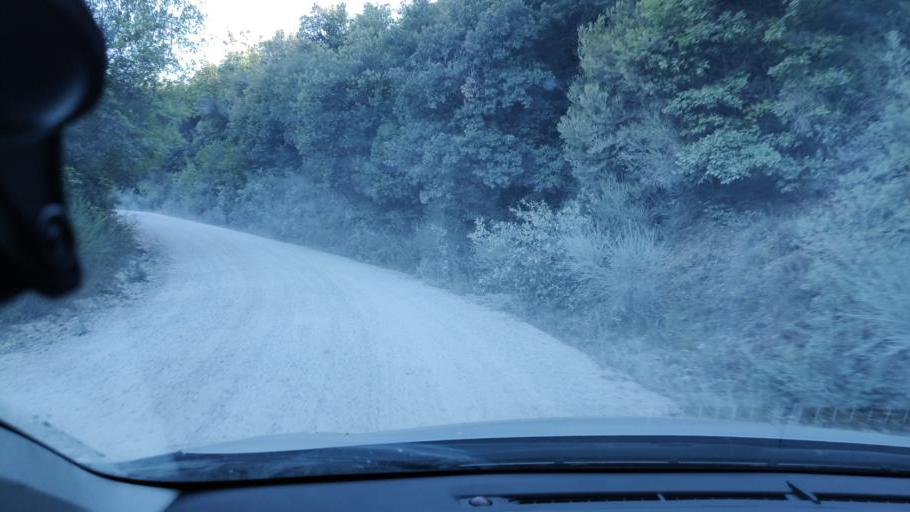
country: IT
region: Umbria
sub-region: Provincia di Terni
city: Amelia
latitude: 42.5359
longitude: 12.3808
